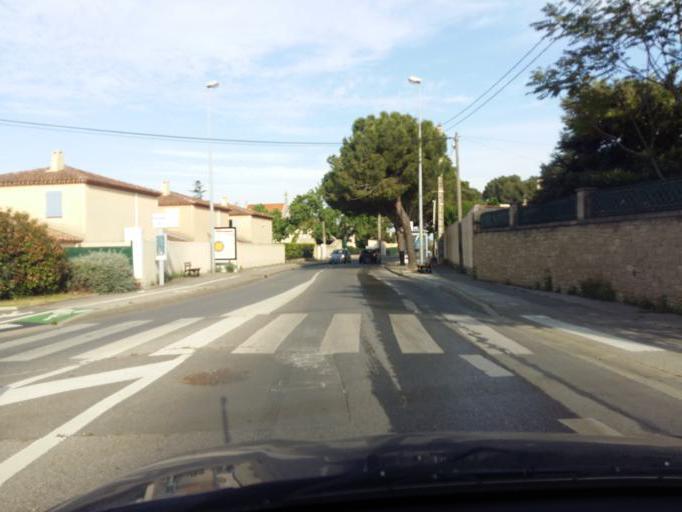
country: FR
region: Provence-Alpes-Cote d'Azur
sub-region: Departement des Bouches-du-Rhone
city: Salon-de-Provence
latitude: 43.6400
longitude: 5.1080
